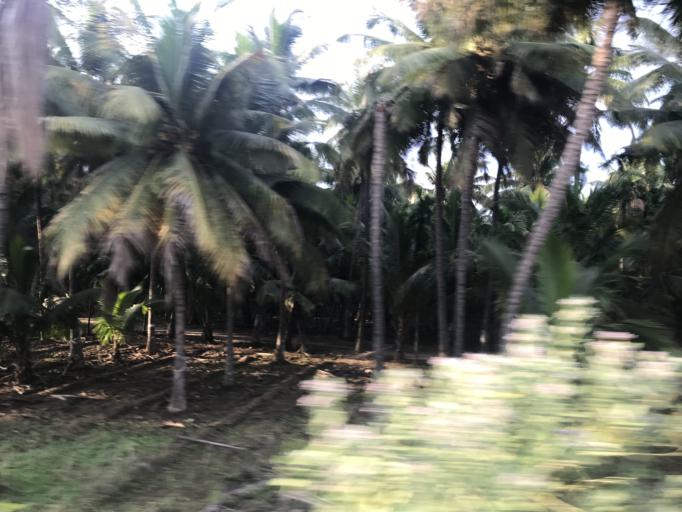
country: IN
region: Tamil Nadu
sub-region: Coimbatore
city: Coimbatore
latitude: 11.0277
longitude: 76.9779
